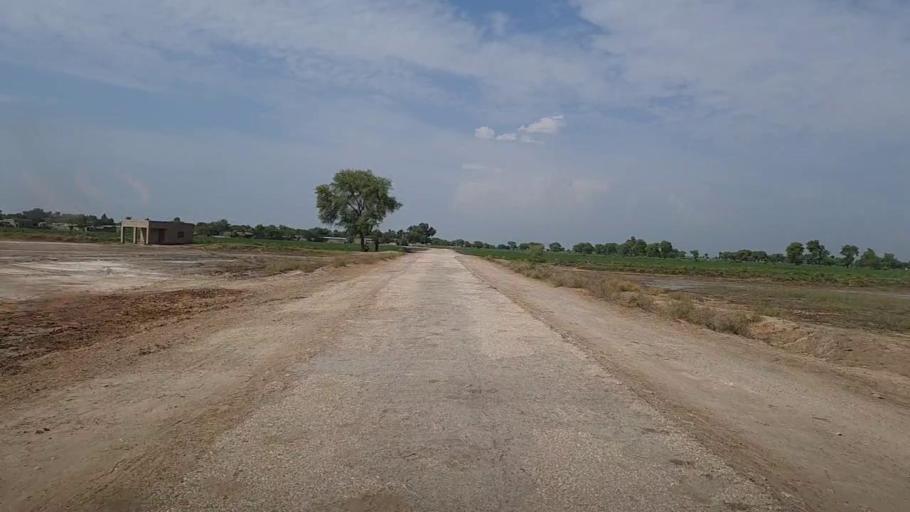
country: PK
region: Sindh
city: Thul
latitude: 28.2416
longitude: 68.8101
